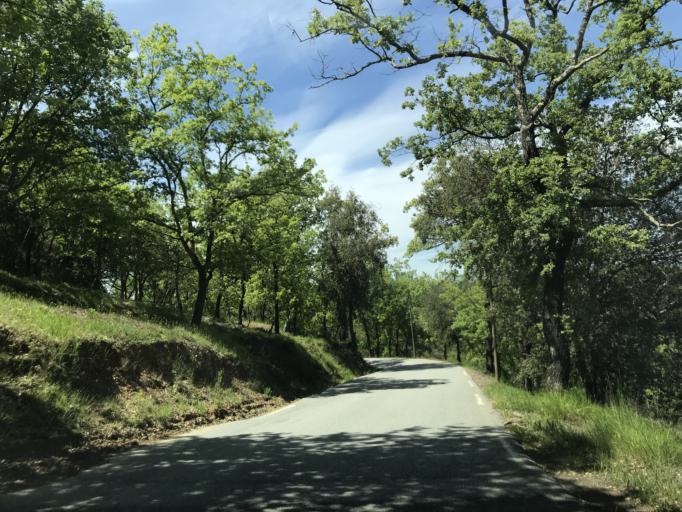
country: FR
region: Provence-Alpes-Cote d'Azur
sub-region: Departement du Var
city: Tanneron
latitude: 43.5847
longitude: 6.8227
